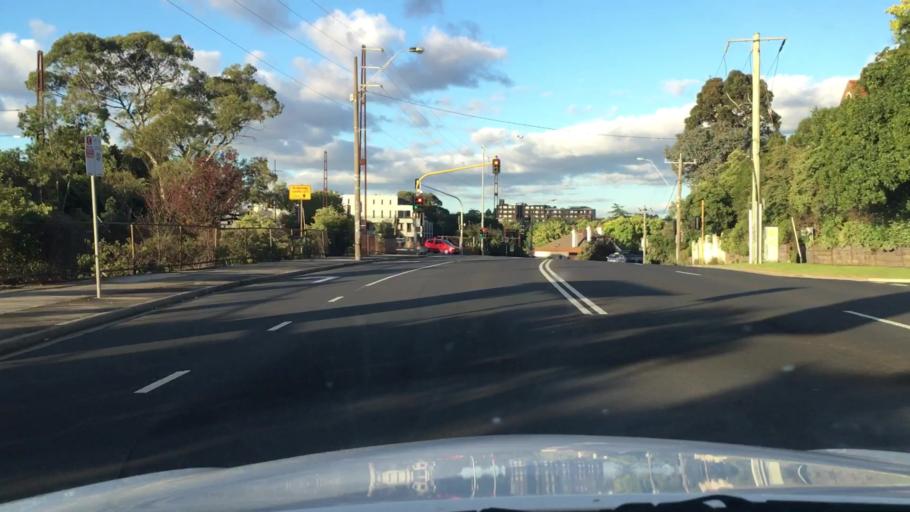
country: AU
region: Victoria
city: Alphington
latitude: -37.7733
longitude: 145.0402
